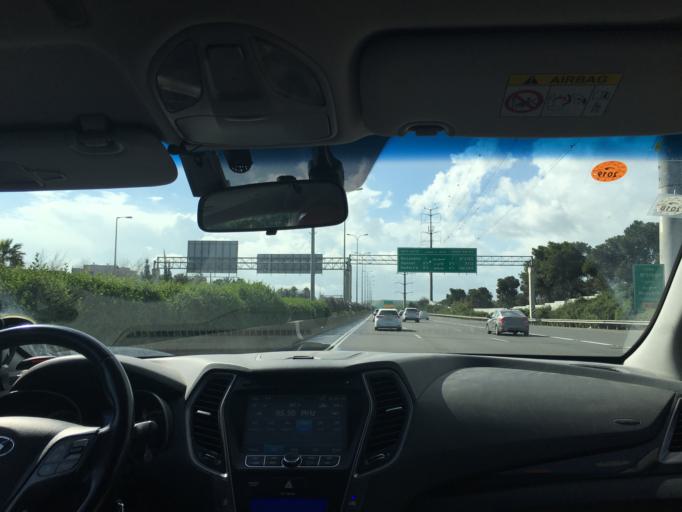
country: IL
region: Tel Aviv
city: Giv`atayim
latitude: 32.0514
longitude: 34.8319
